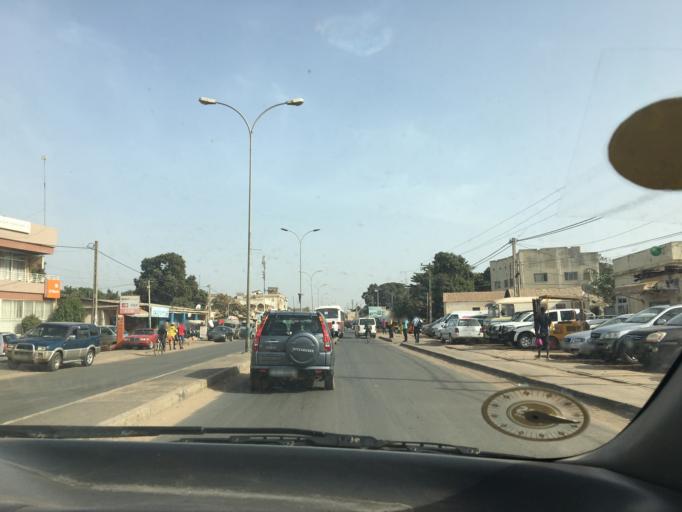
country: GM
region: Western
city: Abuko
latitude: 13.4352
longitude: -16.6763
